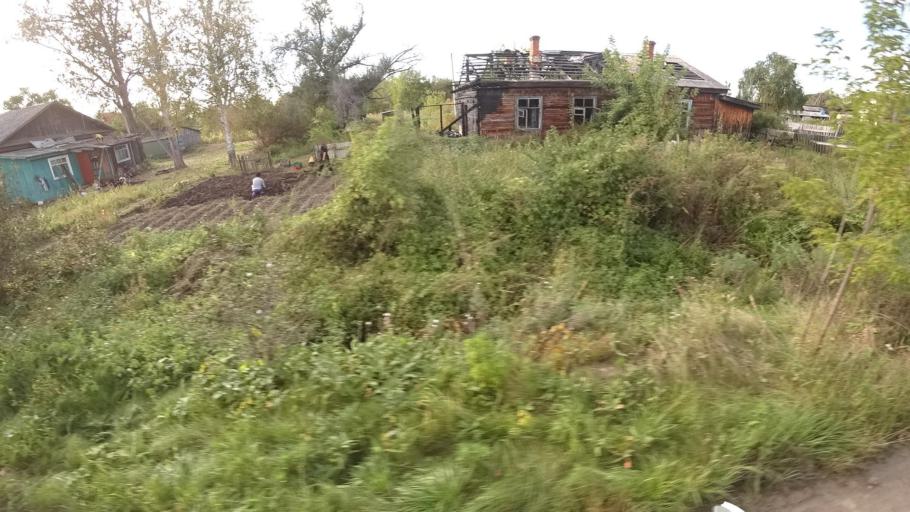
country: RU
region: Primorskiy
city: Dostoyevka
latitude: 44.2871
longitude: 133.4290
